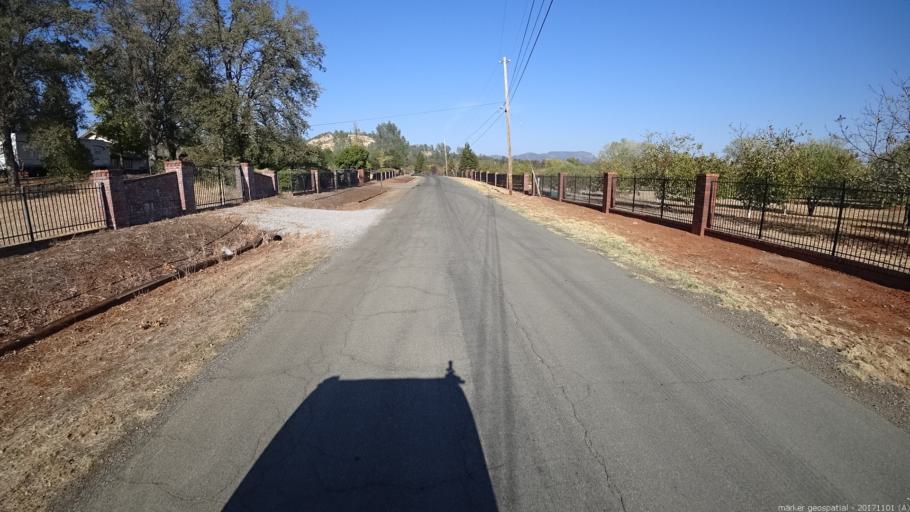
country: US
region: California
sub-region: Shasta County
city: Shasta Lake
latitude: 40.6769
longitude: -122.3390
